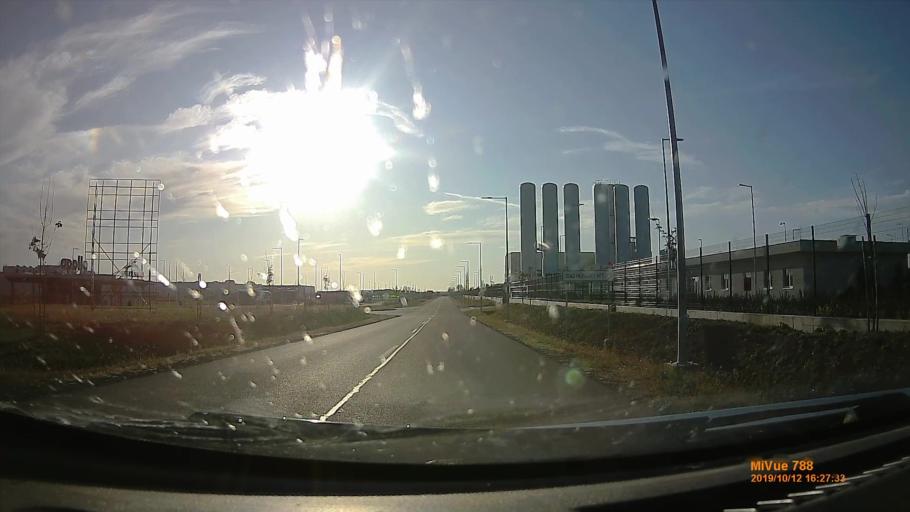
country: HU
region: Heves
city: Adacs
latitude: 47.7246
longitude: 19.9622
